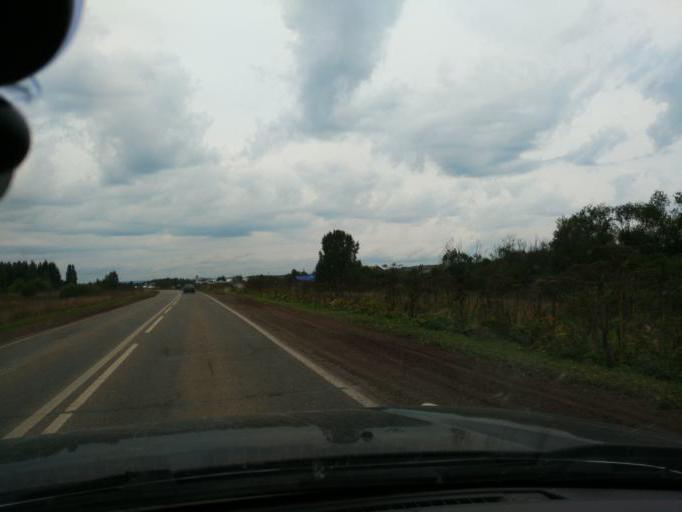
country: RU
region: Perm
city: Chernushka
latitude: 56.7264
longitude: 56.1788
